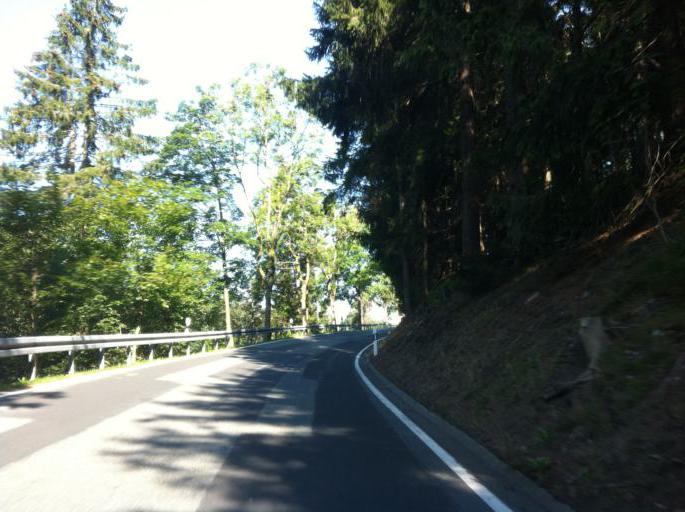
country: DE
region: Thuringia
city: Steinheid
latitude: 50.4721
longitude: 11.0732
